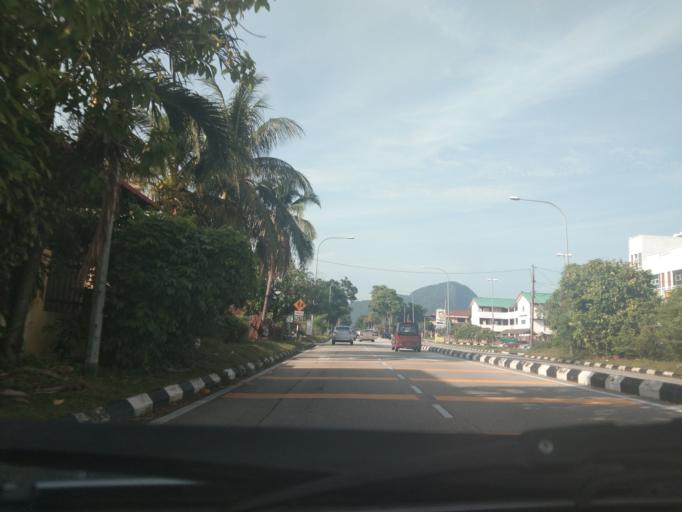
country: MY
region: Perak
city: Ipoh
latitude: 4.5854
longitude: 101.1274
